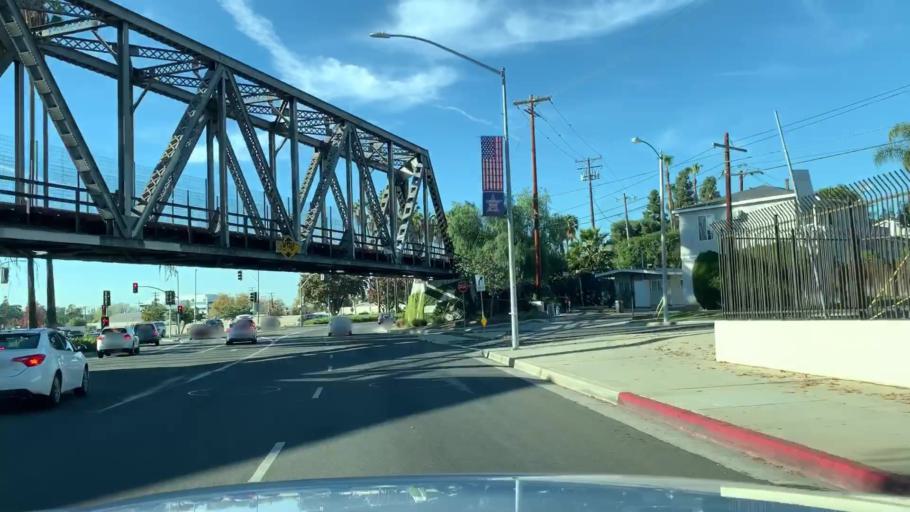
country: US
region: California
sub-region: Los Angeles County
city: South Whittier
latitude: 33.9680
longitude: -118.0412
